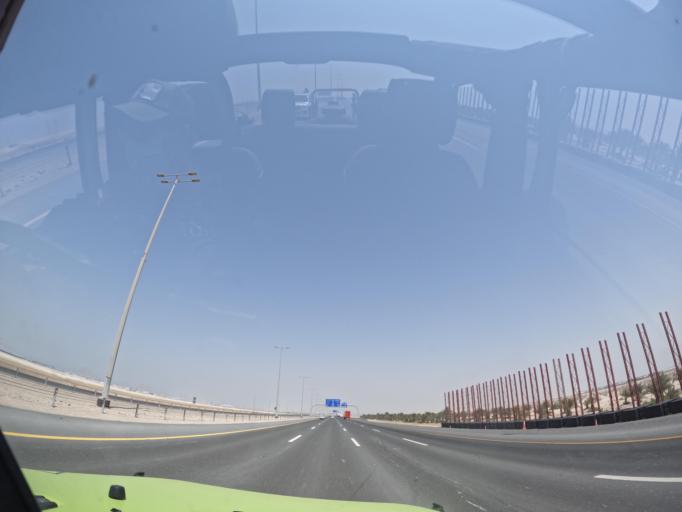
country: AE
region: Abu Dhabi
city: Abu Dhabi
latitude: 24.2374
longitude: 54.4633
